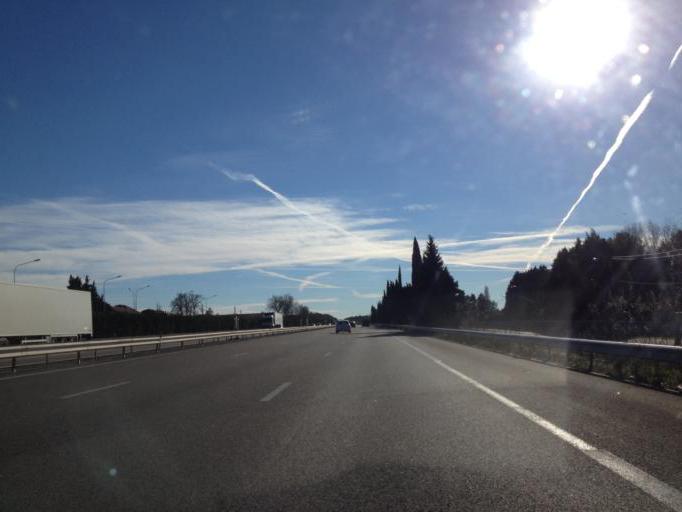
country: FR
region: Provence-Alpes-Cote d'Azur
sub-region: Departement du Vaucluse
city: Courthezon
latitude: 44.0829
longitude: 4.8790
